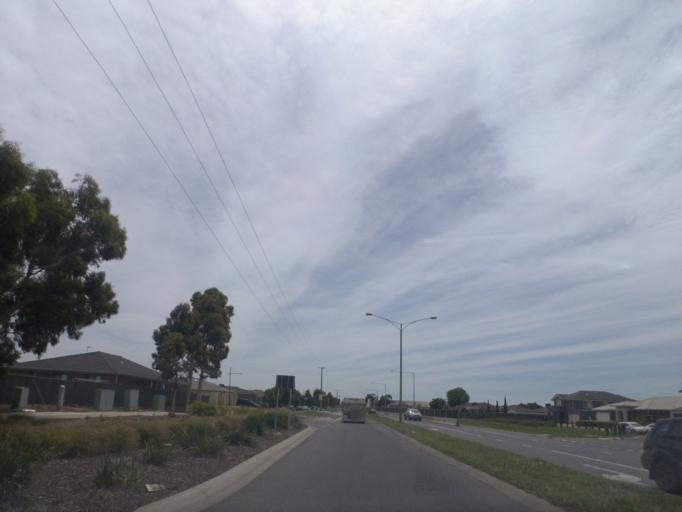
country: AU
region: Victoria
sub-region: Wyndham
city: Tarneit
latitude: -37.8409
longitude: 144.6897
